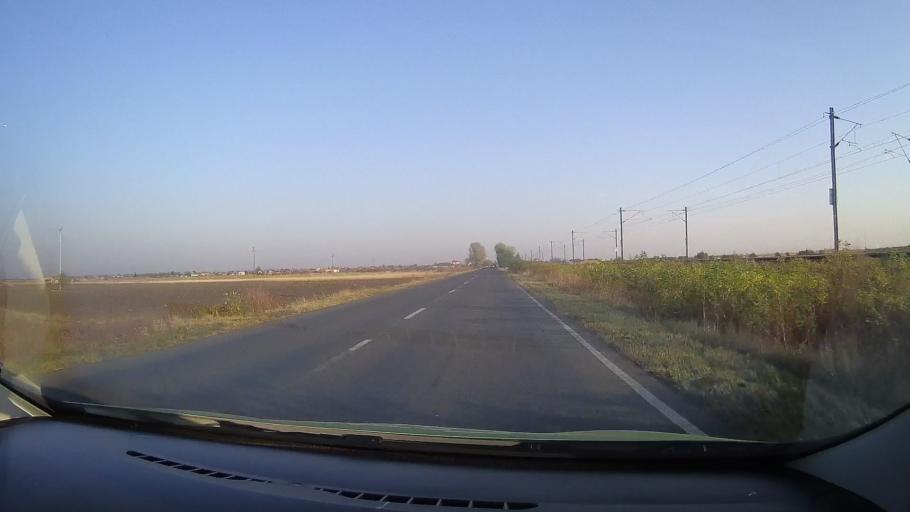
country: RO
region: Arad
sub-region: Comuna Sofronea
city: Sofronea
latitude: 46.2650
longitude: 21.3165
